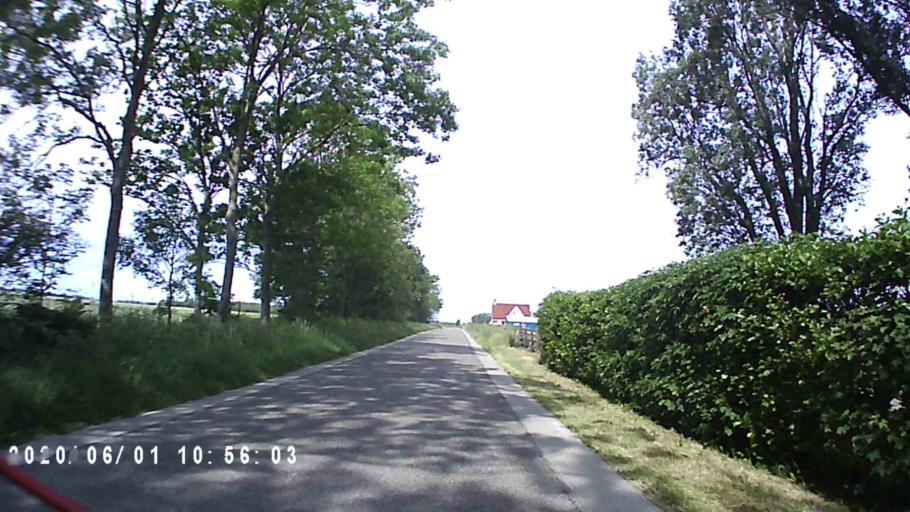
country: NL
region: Friesland
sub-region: Gemeente Franekeradeel
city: Sexbierum
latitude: 53.1988
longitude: 5.5008
